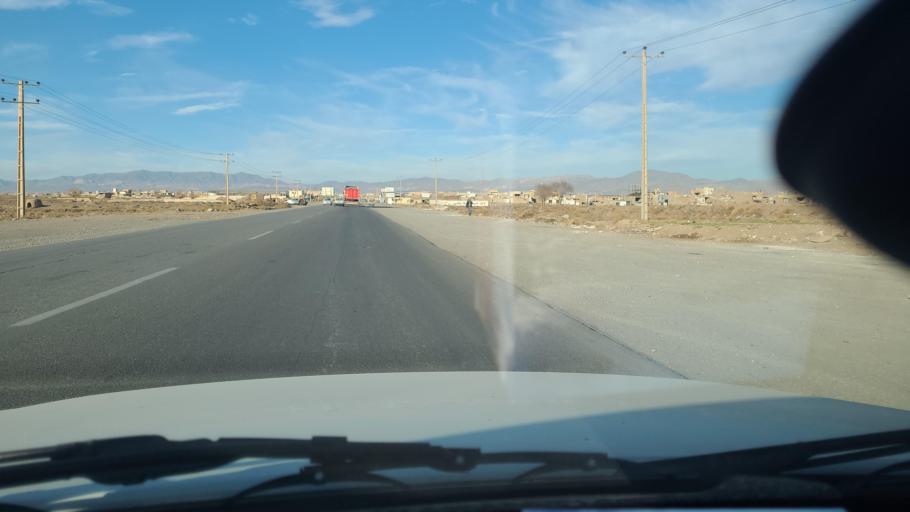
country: IR
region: Razavi Khorasan
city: Sabzevar
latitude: 36.2092
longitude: 57.6504
